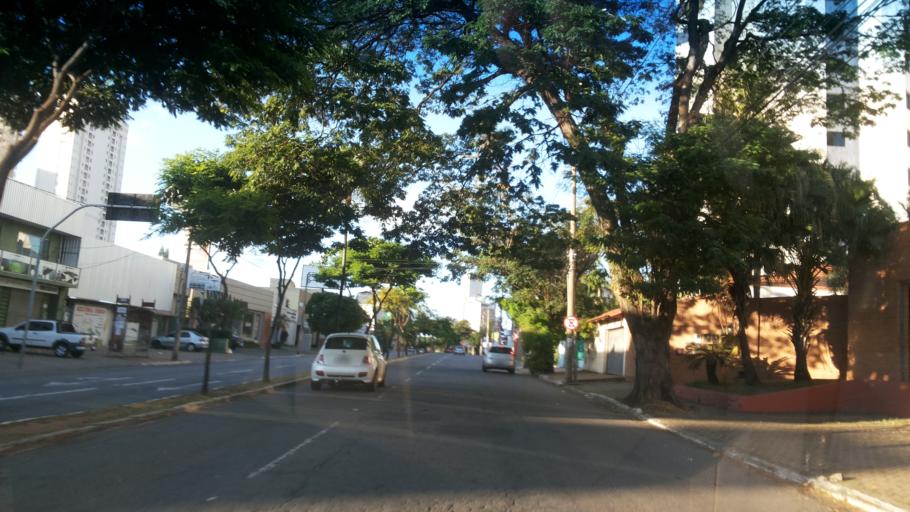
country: BR
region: Goias
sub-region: Goiania
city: Goiania
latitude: -16.6987
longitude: -49.2677
